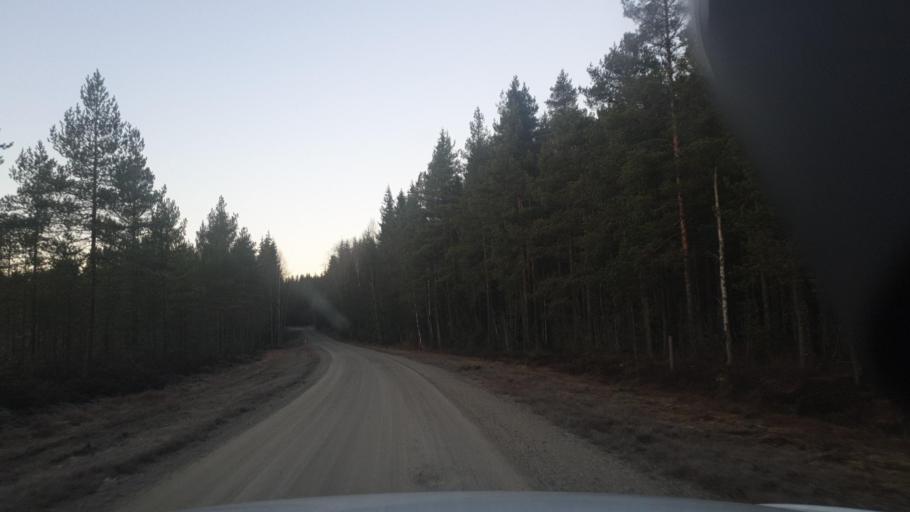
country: SE
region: Vaermland
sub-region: Eda Kommun
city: Charlottenberg
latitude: 59.9822
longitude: 12.4902
